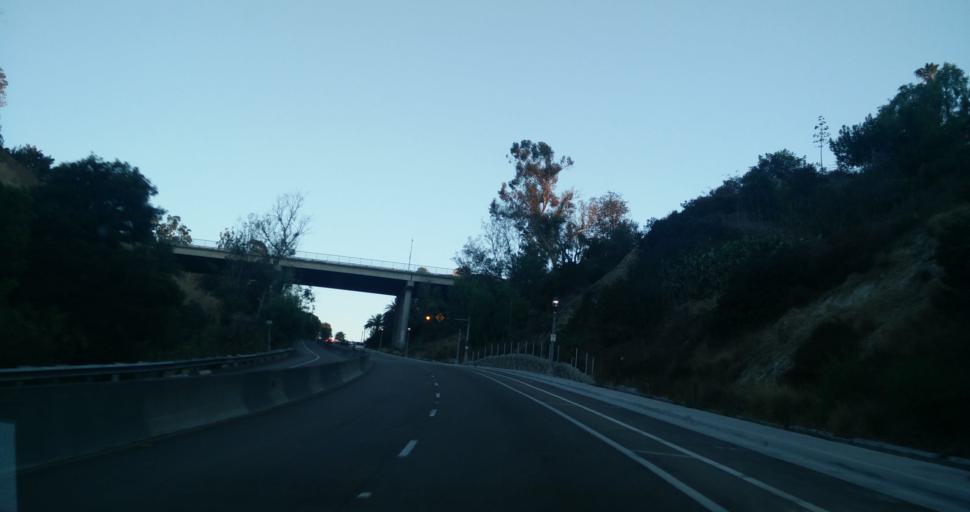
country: US
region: California
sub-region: San Diego County
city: San Diego
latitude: 32.7646
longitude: -117.1392
